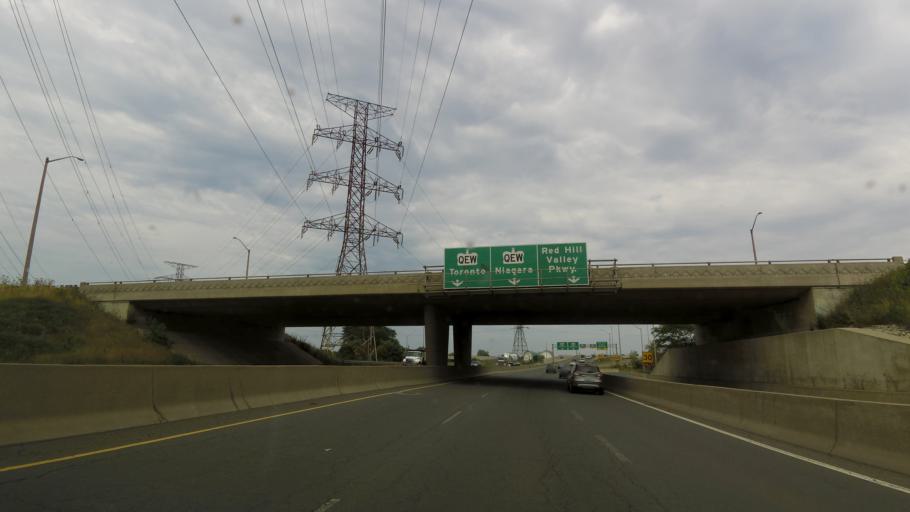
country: CA
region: Ontario
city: Hamilton
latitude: 43.2587
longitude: -79.7736
